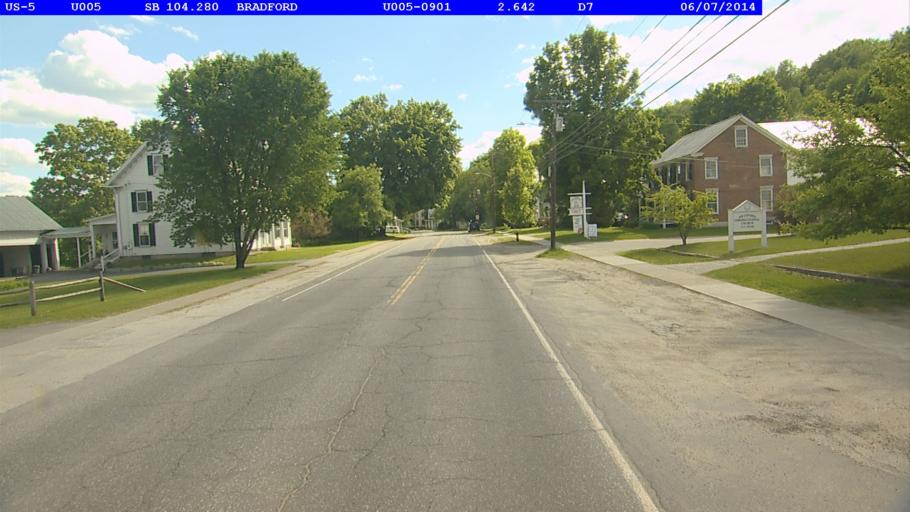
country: US
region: New Hampshire
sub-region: Grafton County
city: Haverhill
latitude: 43.9975
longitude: -72.1267
